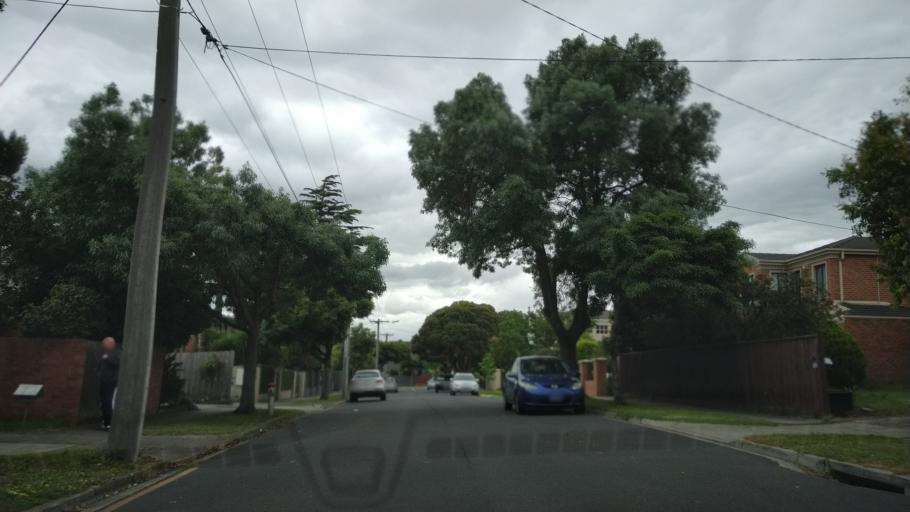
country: AU
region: Victoria
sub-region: Glen Eira
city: Caulfield
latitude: -37.8866
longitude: 145.0324
